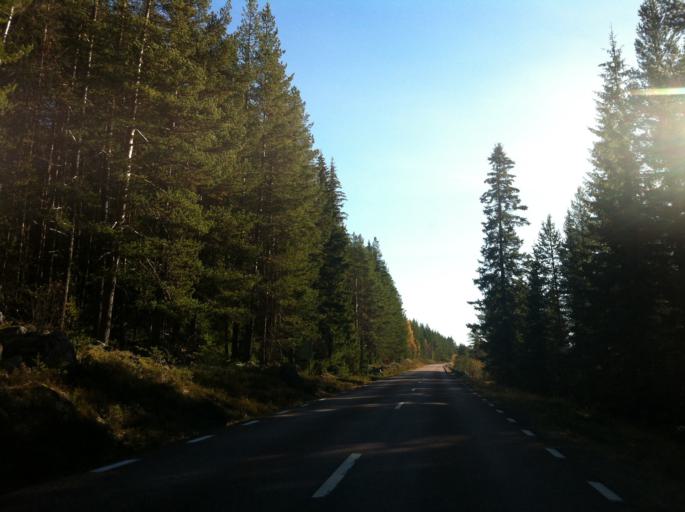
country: NO
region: Hedmark
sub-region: Trysil
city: Innbygda
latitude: 61.8251
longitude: 12.8811
